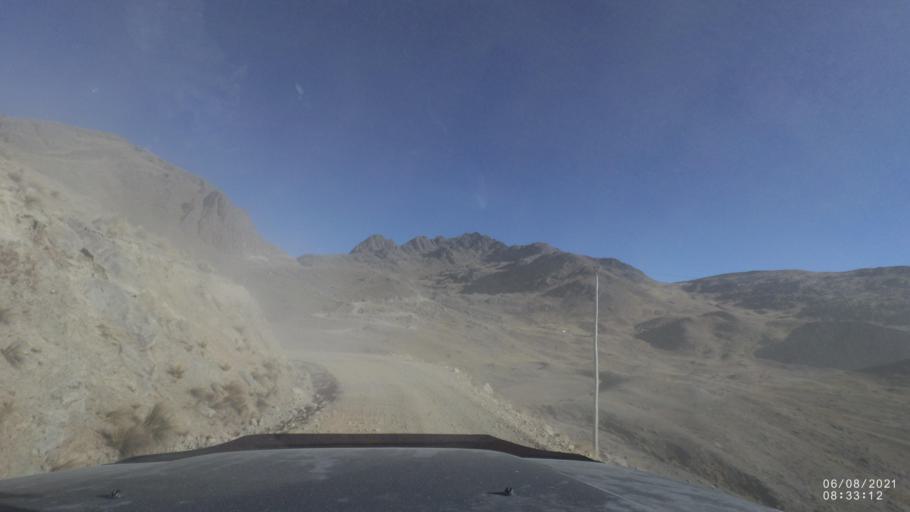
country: BO
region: Cochabamba
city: Sipe Sipe
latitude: -17.1808
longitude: -66.3763
